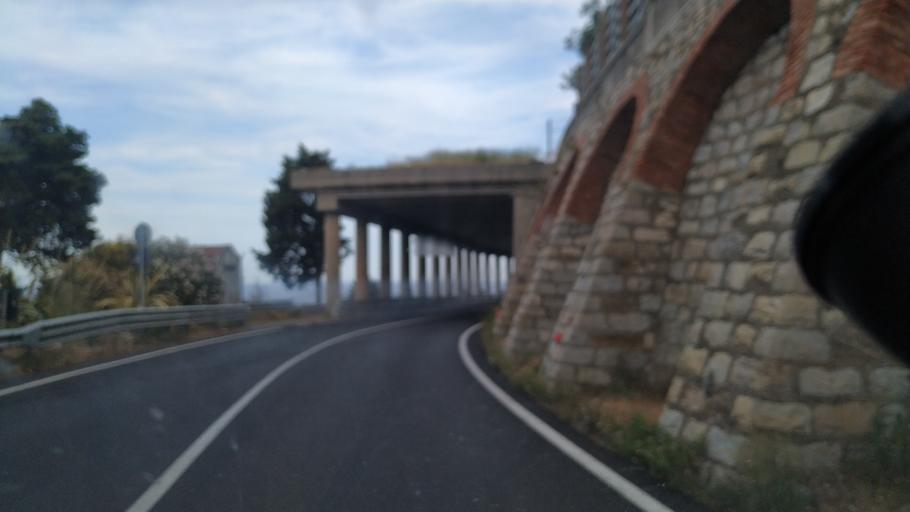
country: IT
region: Liguria
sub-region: Provincia di Savona
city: Marina di Andora
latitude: 43.9574
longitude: 8.1729
